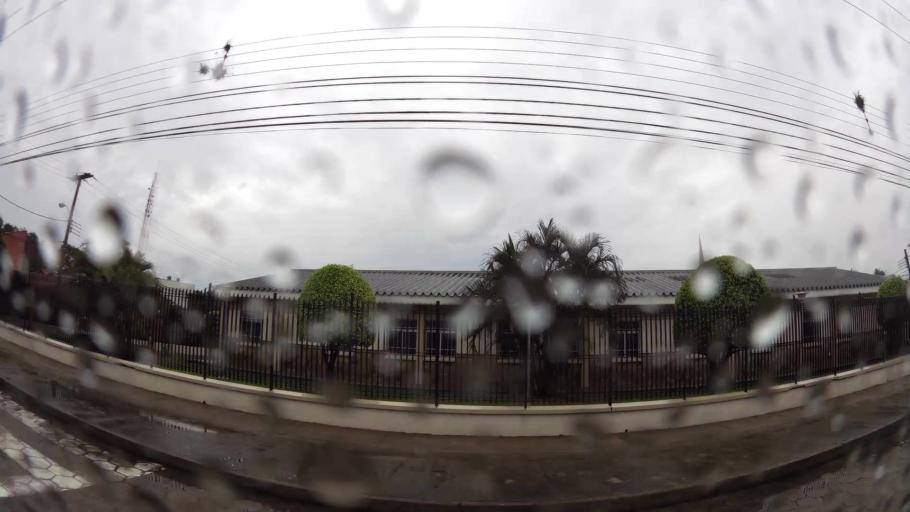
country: BO
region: Santa Cruz
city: Santa Cruz de la Sierra
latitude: -17.7907
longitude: -63.2093
